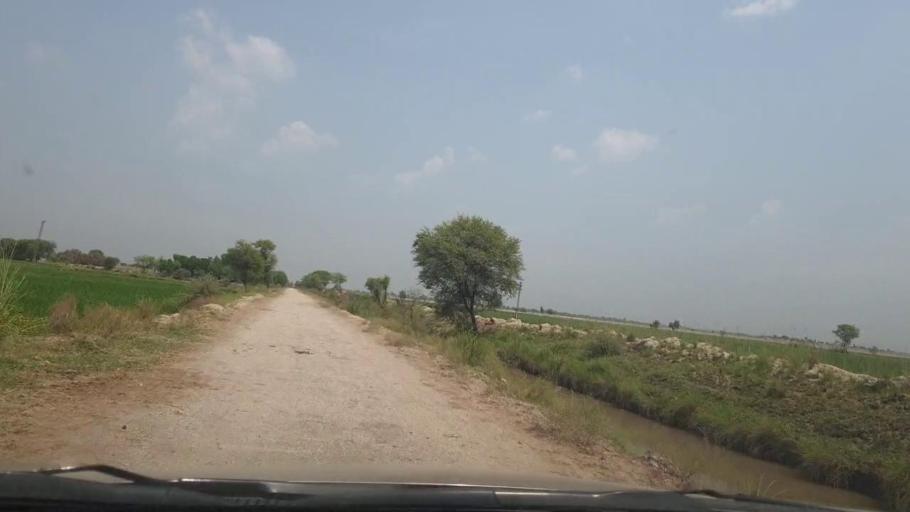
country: PK
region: Sindh
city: Ratodero
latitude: 27.6943
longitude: 68.2331
